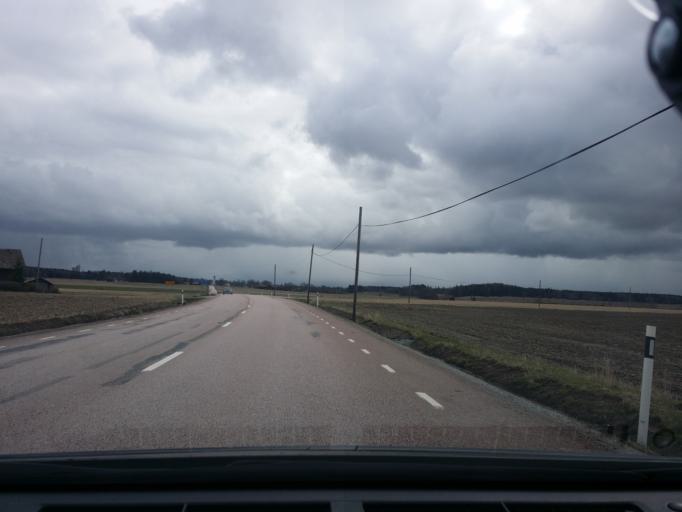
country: SE
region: Uppsala
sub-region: Enkopings Kommun
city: Irsta
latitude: 59.7775
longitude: 16.8593
